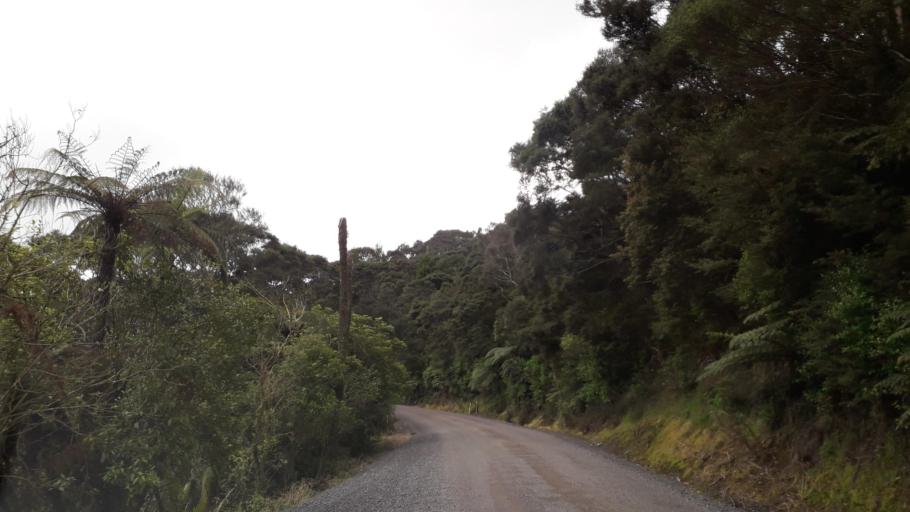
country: NZ
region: Northland
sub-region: Far North District
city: Paihia
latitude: -35.3193
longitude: 174.2328
